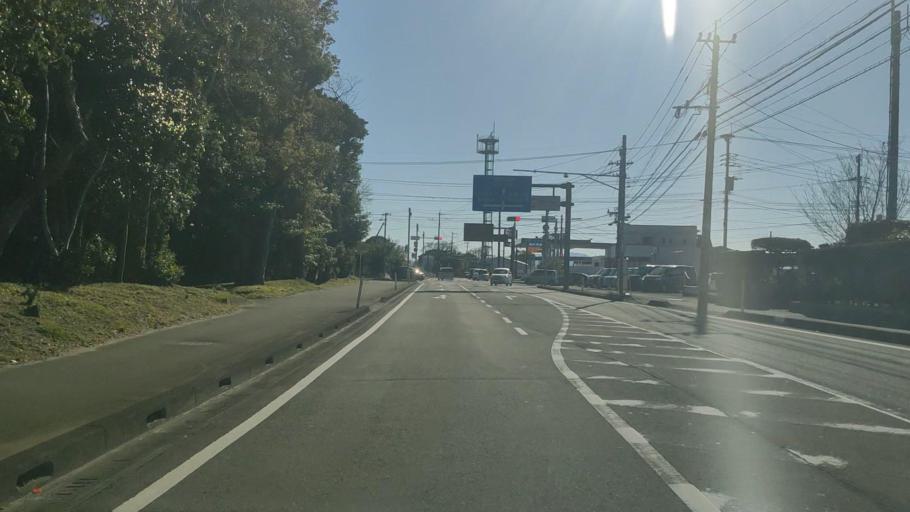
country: JP
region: Miyazaki
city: Miyazaki-shi
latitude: 31.9570
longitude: 131.4630
